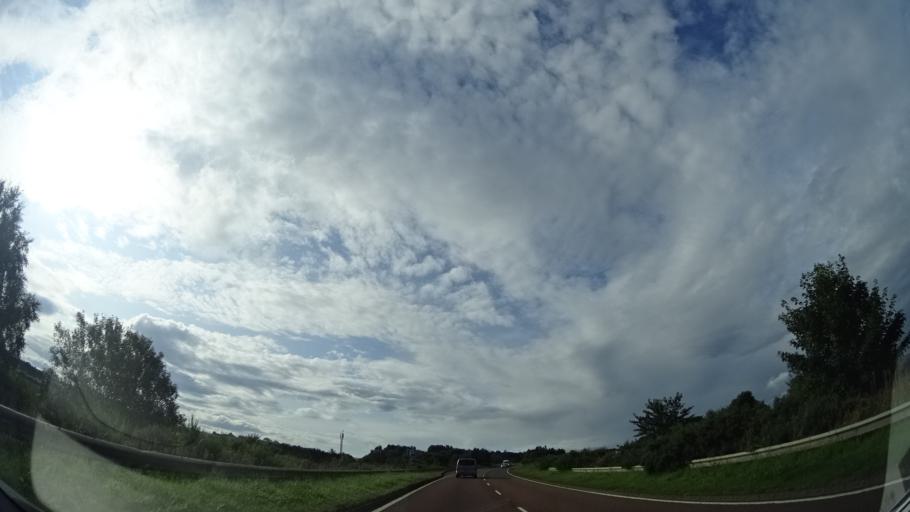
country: GB
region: Scotland
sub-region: Highland
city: Conon Bridge
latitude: 57.5620
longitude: -4.4195
